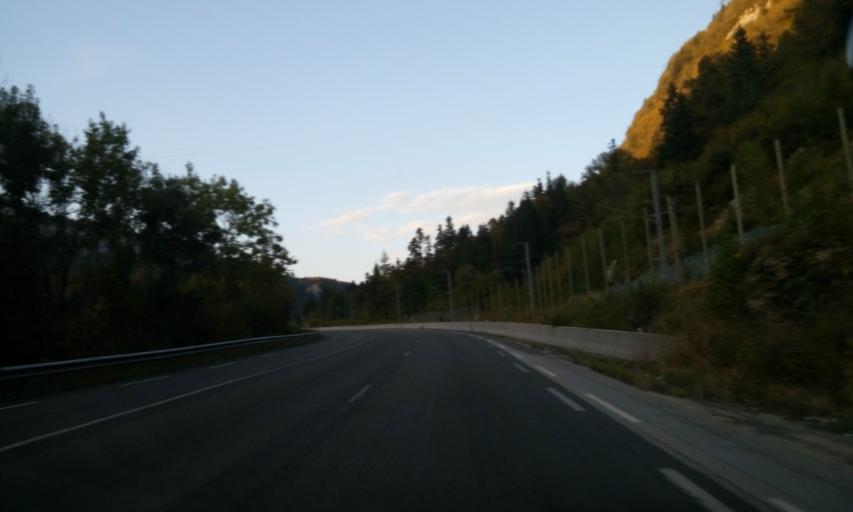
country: FR
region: Rhone-Alpes
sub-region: Departement de l'Ain
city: Nantua
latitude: 46.1501
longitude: 5.6463
